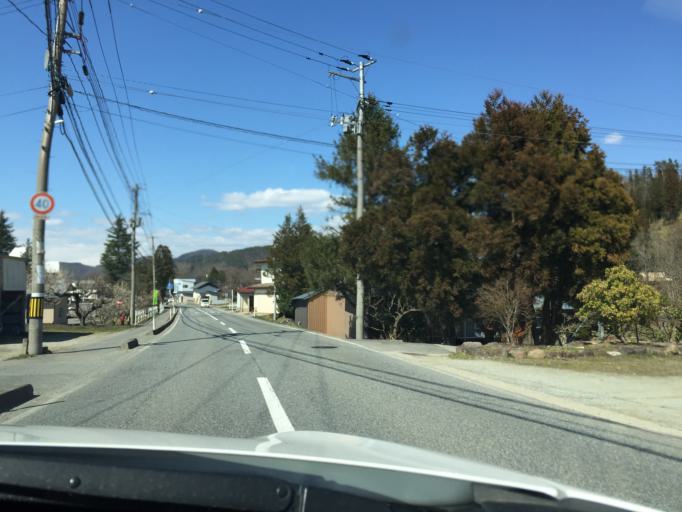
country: JP
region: Yamagata
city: Nagai
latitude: 38.1914
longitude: 140.1009
